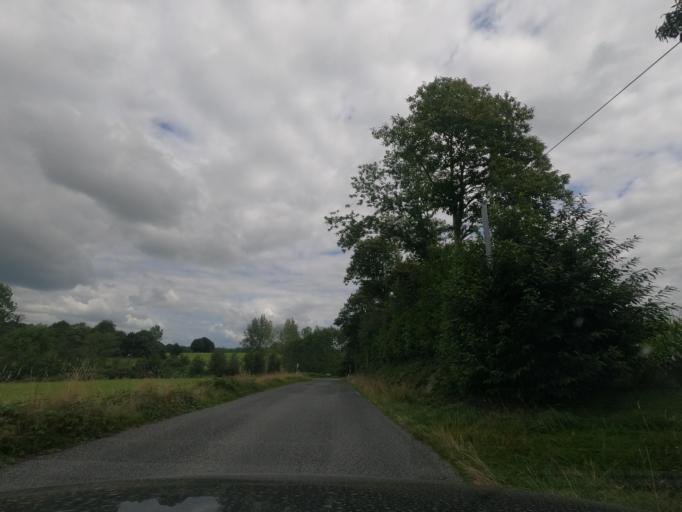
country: FR
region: Pays de la Loire
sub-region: Departement de la Mayenne
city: Fougerolles-du-Plessis
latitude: 48.4996
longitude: -0.9192
